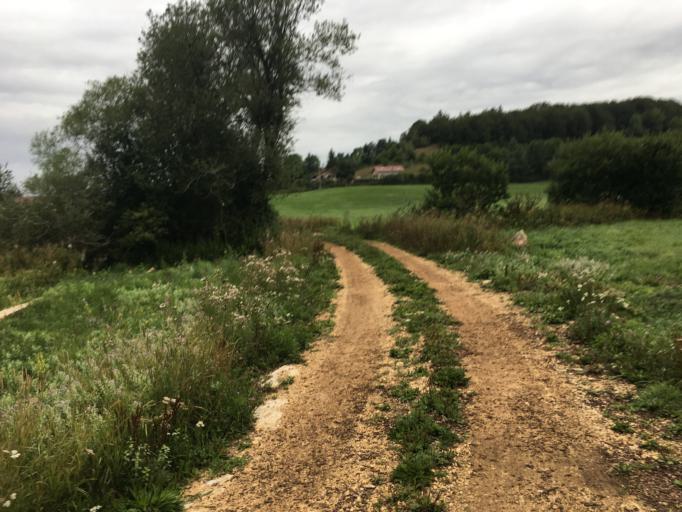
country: FR
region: Franche-Comte
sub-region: Departement du Jura
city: Morbier
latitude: 46.6123
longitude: 5.9751
